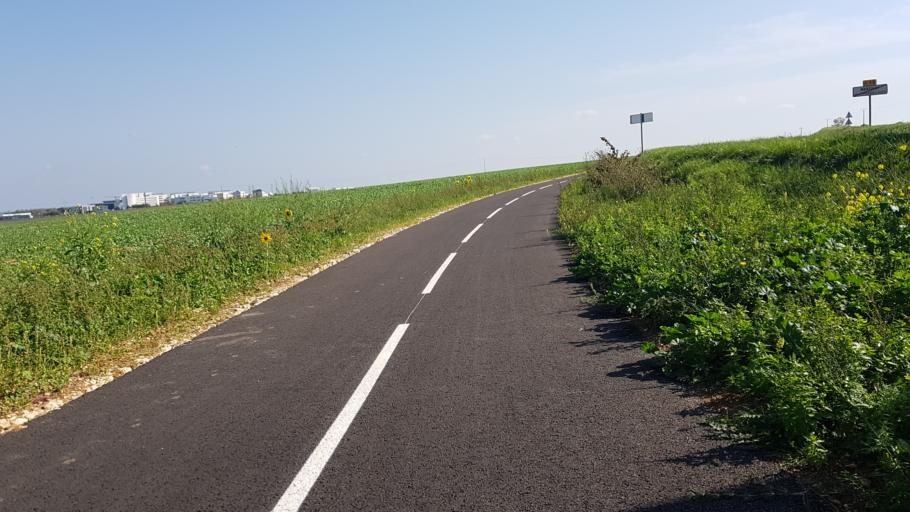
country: FR
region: Poitou-Charentes
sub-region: Departement de la Vienne
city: Chasseneuil-du-Poitou
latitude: 46.6598
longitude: 0.3431
